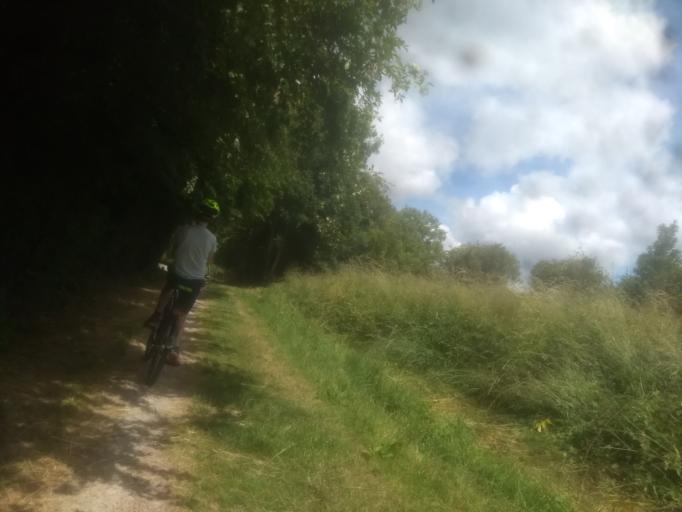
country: FR
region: Nord-Pas-de-Calais
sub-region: Departement du Pas-de-Calais
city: Sainte-Catherine
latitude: 50.3044
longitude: 2.7543
